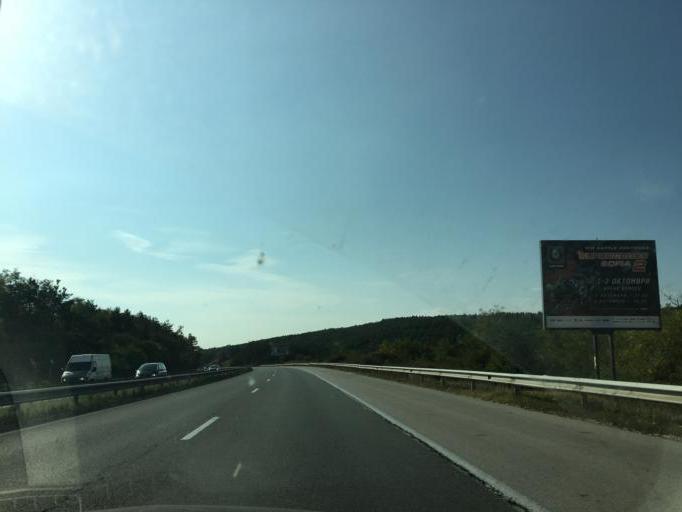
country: BG
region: Sofiya
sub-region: Obshtina Ikhtiman
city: Ikhtiman
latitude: 42.5168
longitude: 23.7524
